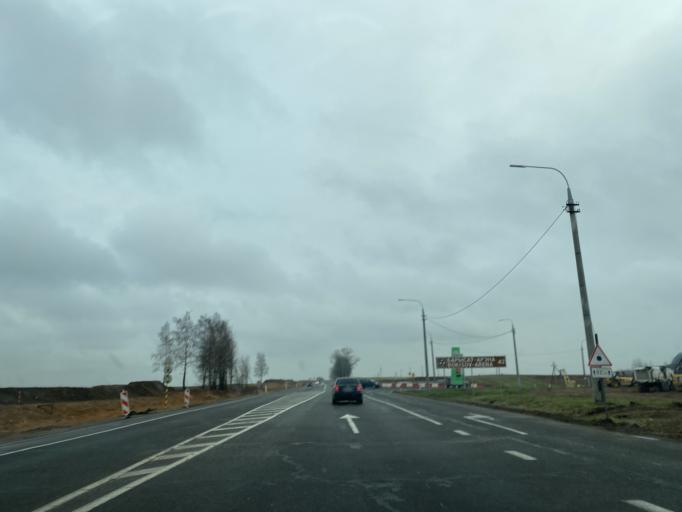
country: BY
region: Minsk
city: Slabada
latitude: 54.0230
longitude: 27.9299
